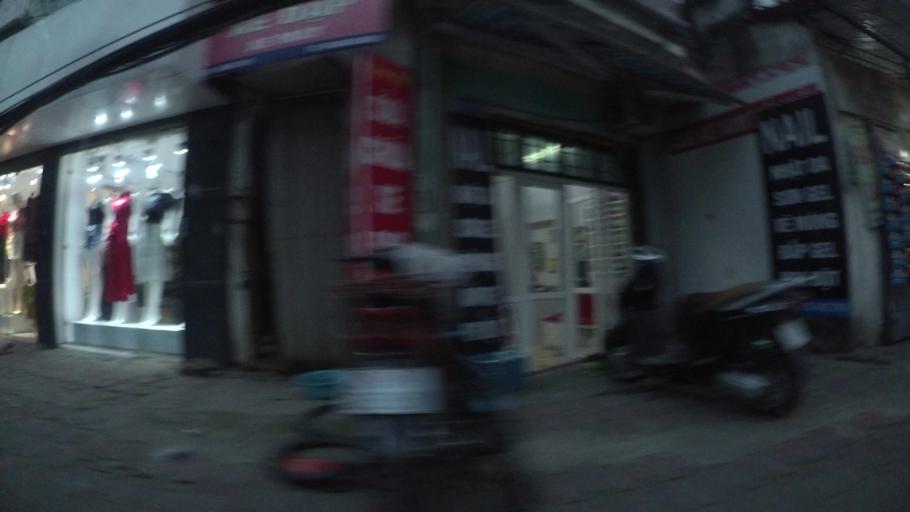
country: VN
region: Ha Noi
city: Ha Dong
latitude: 20.9733
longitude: 105.7852
